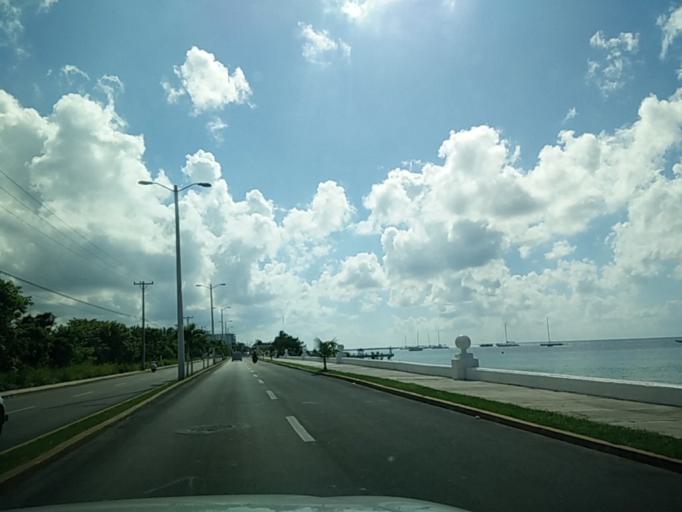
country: MX
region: Quintana Roo
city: San Miguel de Cozumel
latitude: 20.4902
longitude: -86.9670
